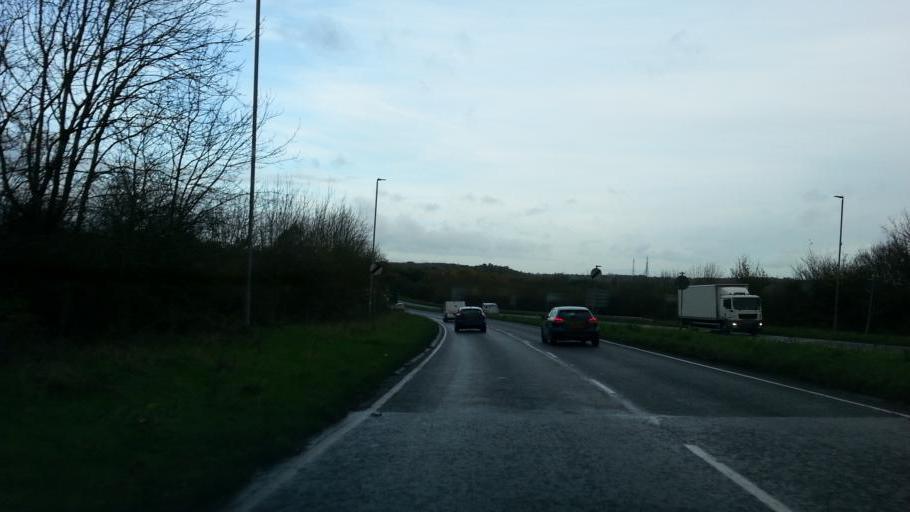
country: GB
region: England
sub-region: Leicestershire
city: Markfield
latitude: 52.6875
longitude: -1.2680
